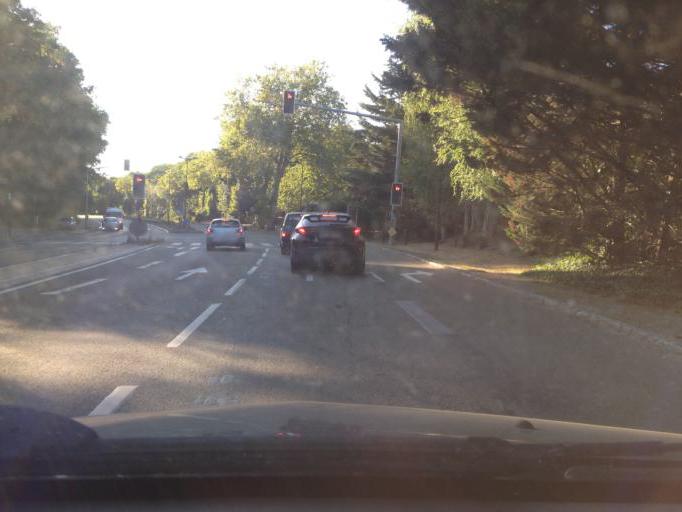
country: FR
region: Ile-de-France
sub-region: Departement des Yvelines
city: Louveciennes
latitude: 48.8716
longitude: 2.1111
